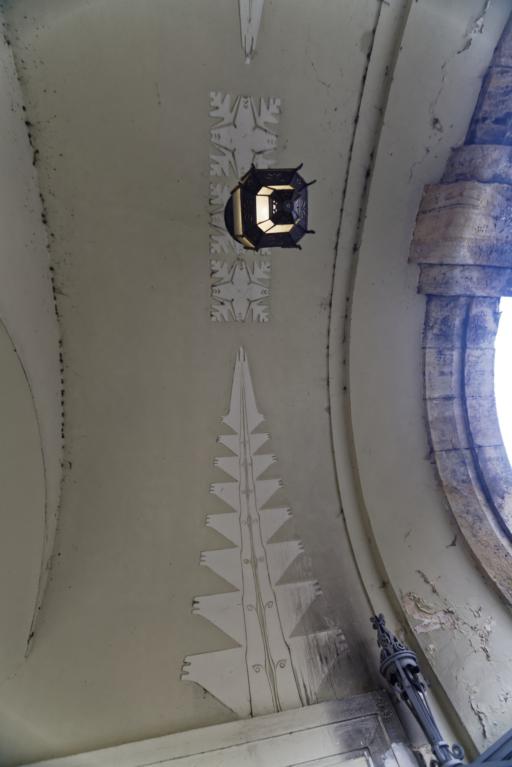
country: CZ
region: Kralovehradecky
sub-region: Okres Hradec Kralove
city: Hradec Kralove
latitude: 50.2108
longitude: 15.8296
